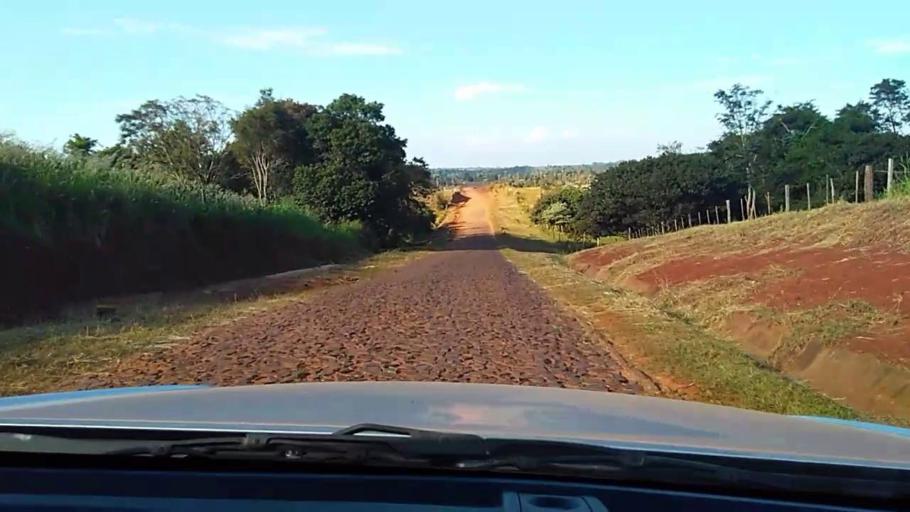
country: PY
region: Alto Parana
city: Doctor Juan Leon Mallorquin
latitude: -25.6987
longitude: -55.3810
